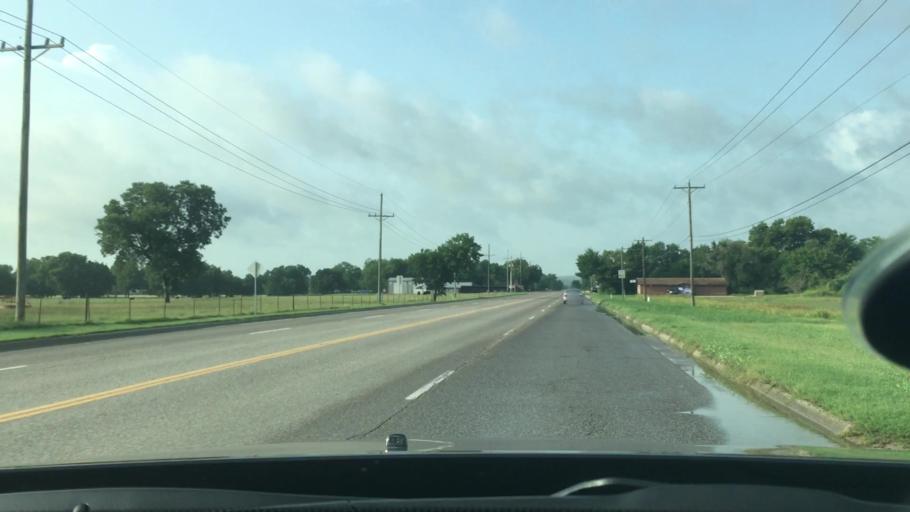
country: US
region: Oklahoma
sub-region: Murray County
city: Davis
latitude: 34.4845
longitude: -97.1306
